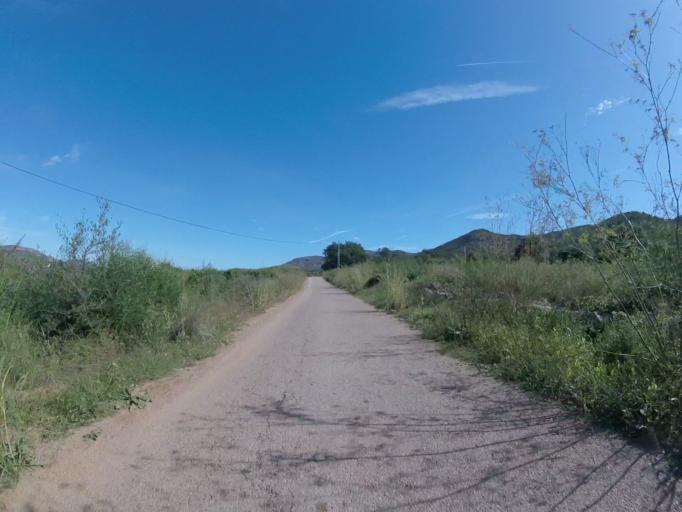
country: ES
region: Valencia
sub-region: Provincia de Castello
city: Santa Magdalena de Pulpis
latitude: 40.3590
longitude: 0.3096
